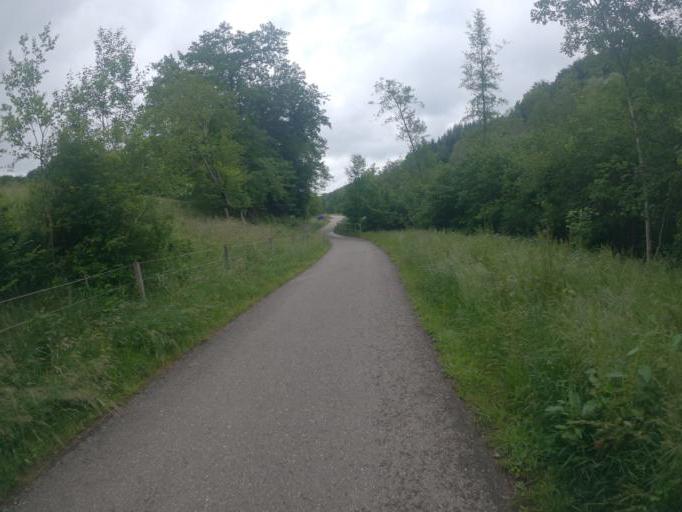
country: DE
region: Baden-Wuerttemberg
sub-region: Regierungsbezirk Stuttgart
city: Ebersbach an der Fils
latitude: 48.7483
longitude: 9.5394
